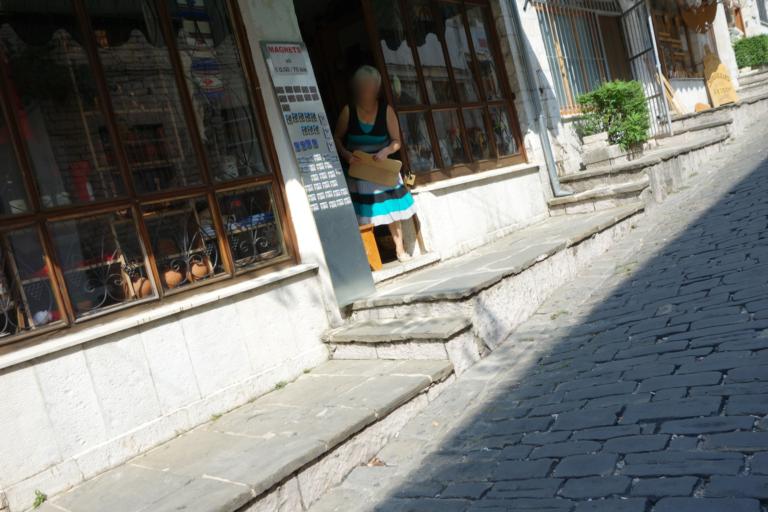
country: AL
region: Gjirokaster
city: Gjirokaster
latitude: 40.0740
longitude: 20.1389
